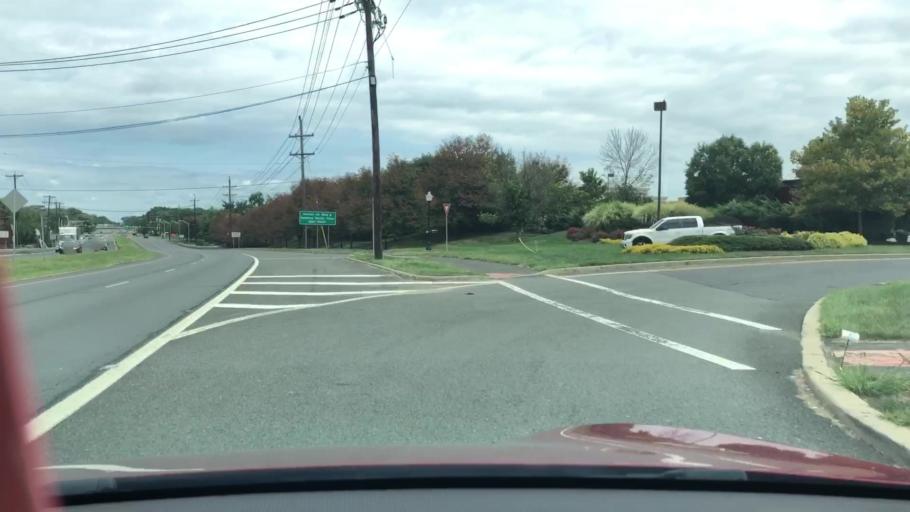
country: US
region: New Jersey
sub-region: Mercer County
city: Yardville
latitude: 40.1947
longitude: -74.6435
